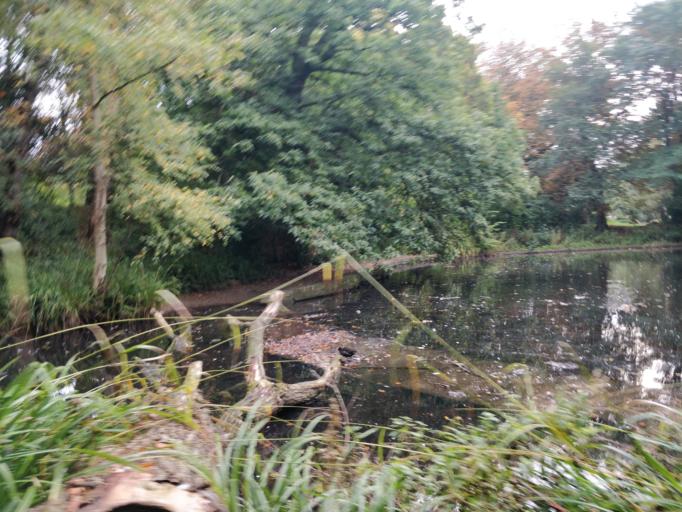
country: GB
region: England
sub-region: Lancashire
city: Banks
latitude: 53.6626
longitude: -2.9602
